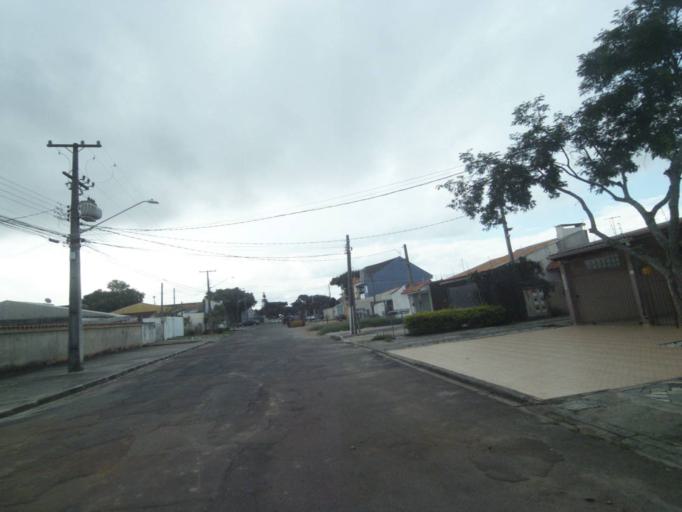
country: BR
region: Parana
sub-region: Pinhais
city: Pinhais
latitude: -25.4580
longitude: -49.2064
